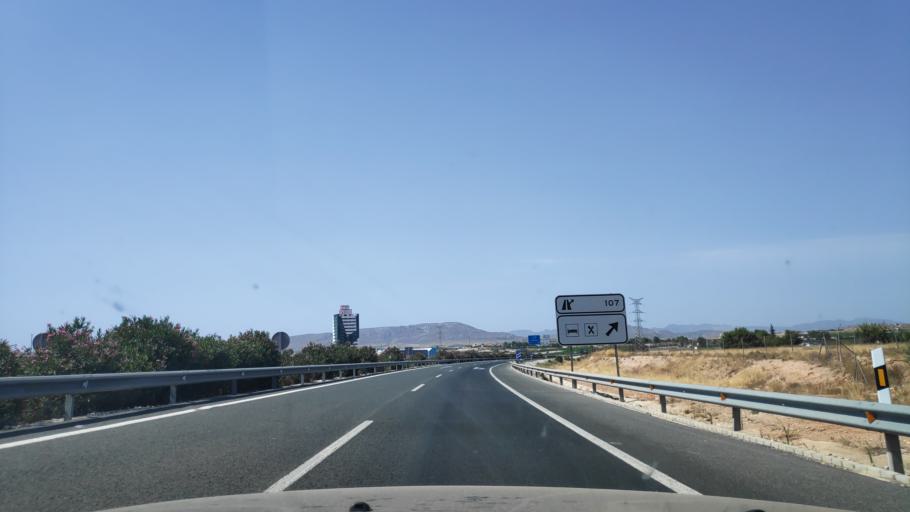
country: ES
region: Murcia
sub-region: Murcia
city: Blanca
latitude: 38.2101
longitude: -1.3512
